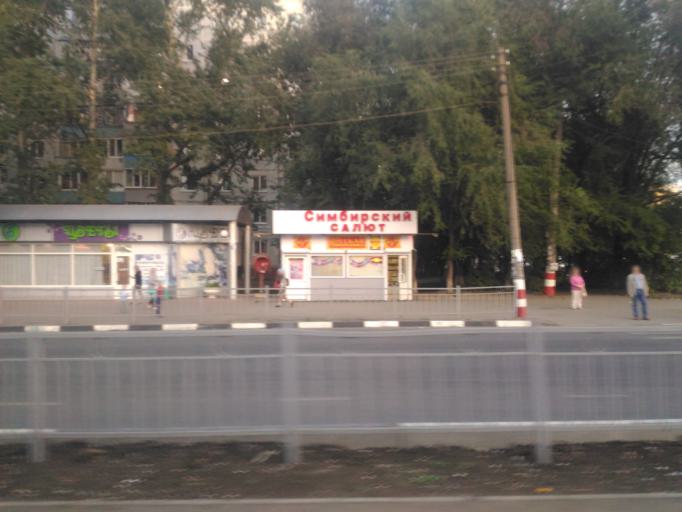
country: RU
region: Ulyanovsk
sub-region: Ulyanovskiy Rayon
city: Ulyanovsk
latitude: 54.2760
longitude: 48.2912
